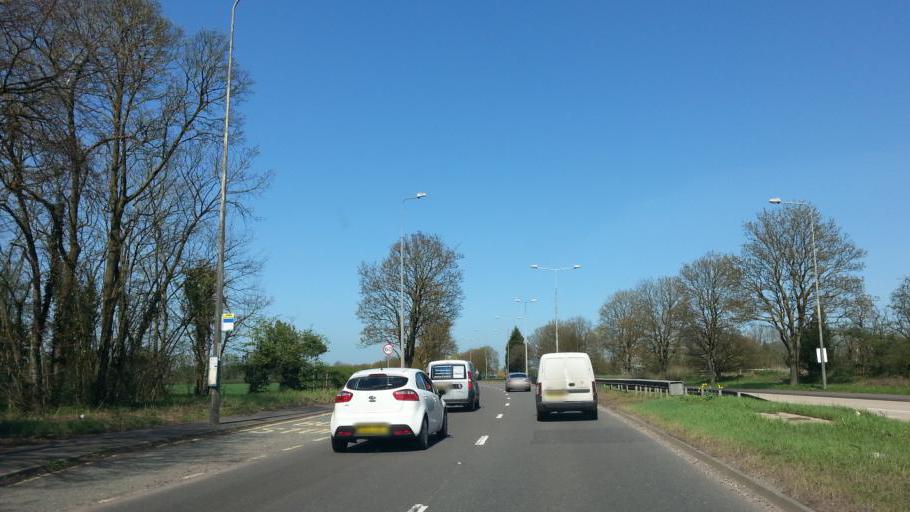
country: GB
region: England
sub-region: Staffordshire
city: Brewood
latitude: 52.6727
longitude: -2.1305
